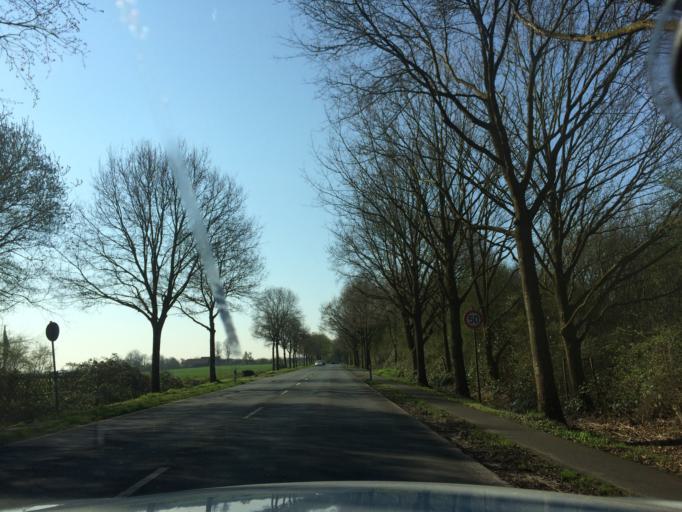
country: DE
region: North Rhine-Westphalia
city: Herten
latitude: 51.5961
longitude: 7.0953
